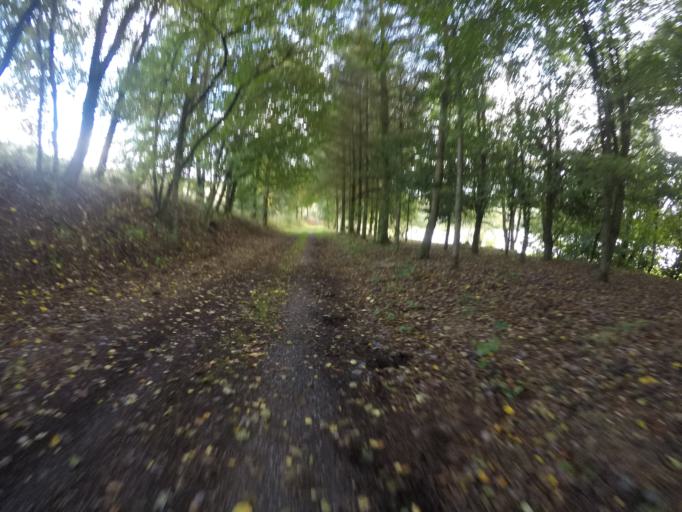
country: BE
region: Wallonia
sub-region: Province du Luxembourg
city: Bastogne
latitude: 49.9324
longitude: 5.6976
